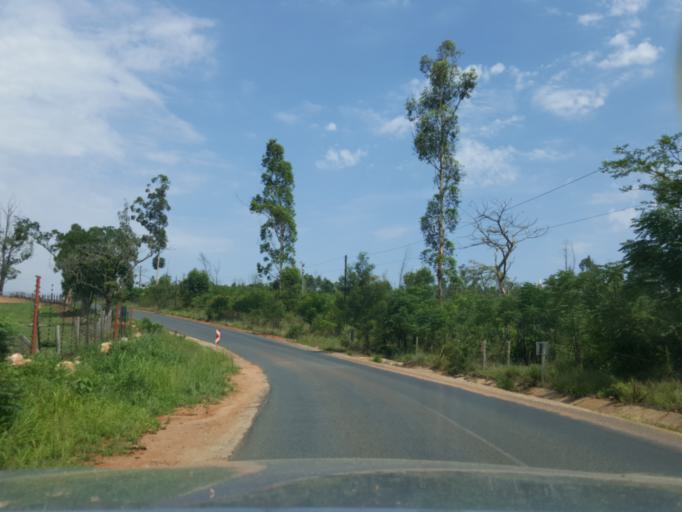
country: ZA
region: Mpumalanga
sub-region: Ehlanzeni District
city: White River
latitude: -25.3253
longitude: 31.0688
